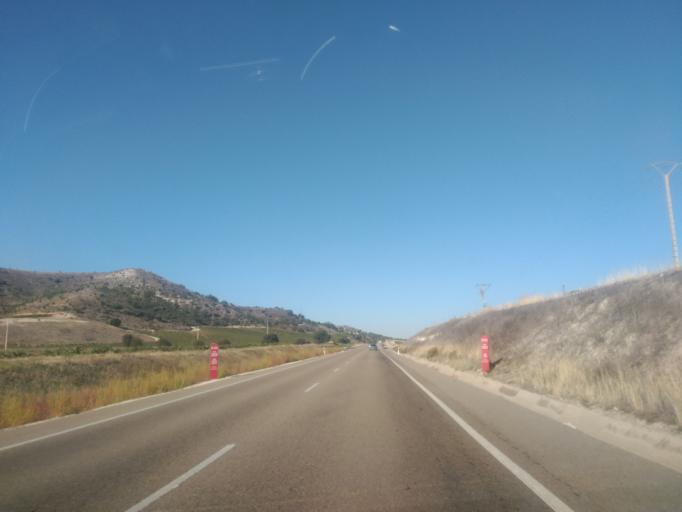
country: ES
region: Castille and Leon
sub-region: Provincia de Valladolid
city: Valbuena de Duero
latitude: 41.6237
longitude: -4.2611
